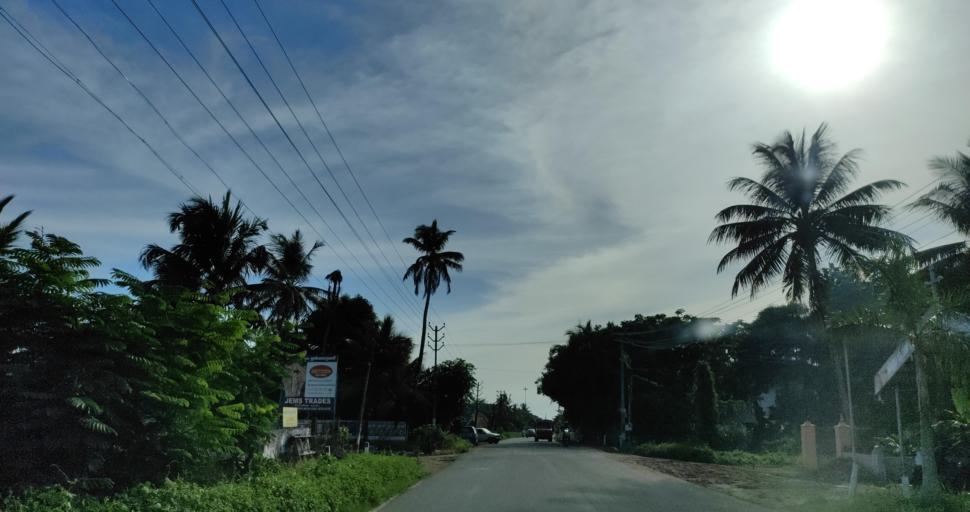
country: IN
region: Kerala
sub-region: Kottayam
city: Kottayam
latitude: 9.5928
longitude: 76.4512
